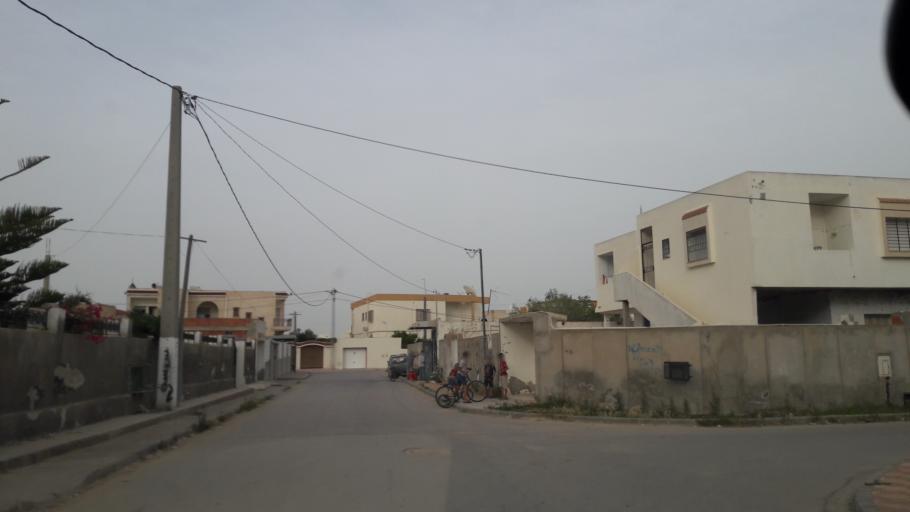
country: TN
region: Safaqis
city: Al Qarmadah
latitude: 34.7773
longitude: 10.7657
